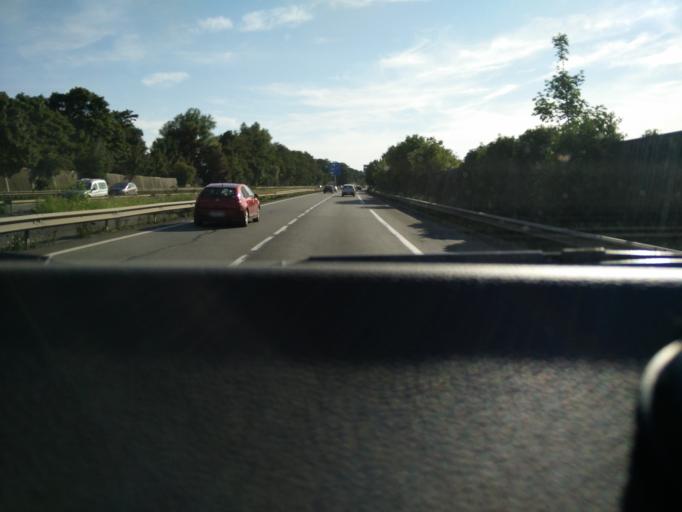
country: FR
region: Nord-Pas-de-Calais
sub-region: Departement du Nord
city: Wavrechain-sous-Denain
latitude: 50.3189
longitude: 3.4198
